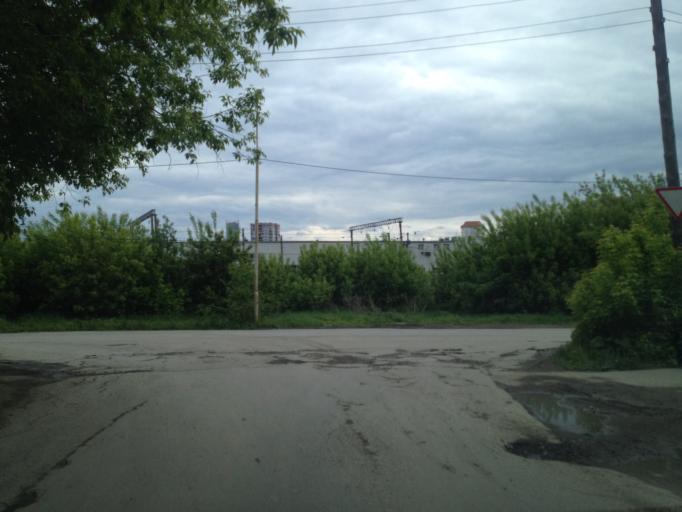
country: RU
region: Sverdlovsk
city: Yekaterinburg
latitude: 56.8605
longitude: 60.5826
